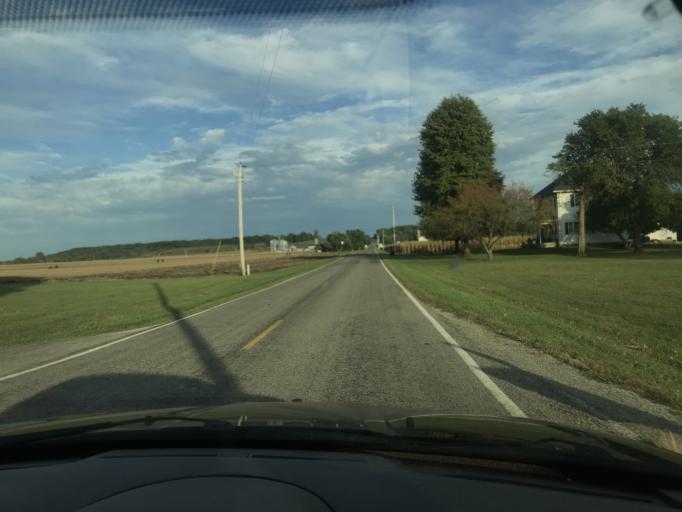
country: US
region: Ohio
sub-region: Logan County
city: West Liberty
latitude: 40.1941
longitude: -83.7871
